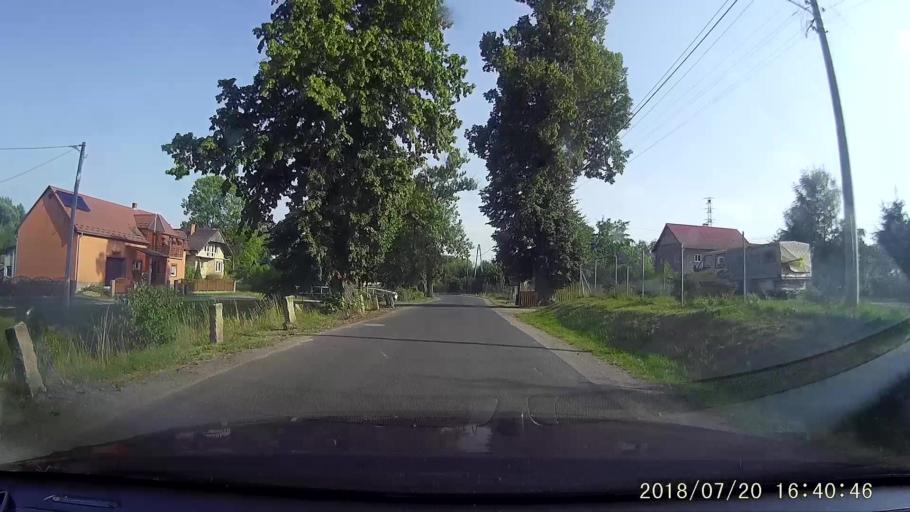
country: PL
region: Lower Silesian Voivodeship
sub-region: Powiat lubanski
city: Siekierczyn
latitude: 51.0841
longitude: 15.1487
